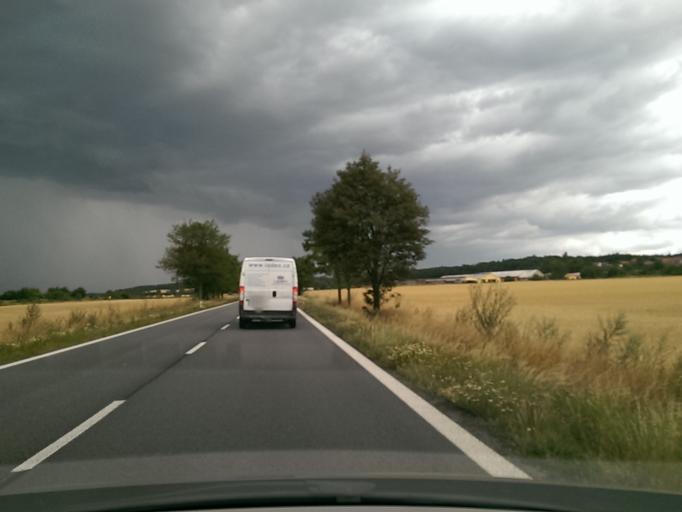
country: CZ
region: Central Bohemia
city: Loucen
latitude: 50.2506
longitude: 14.9975
